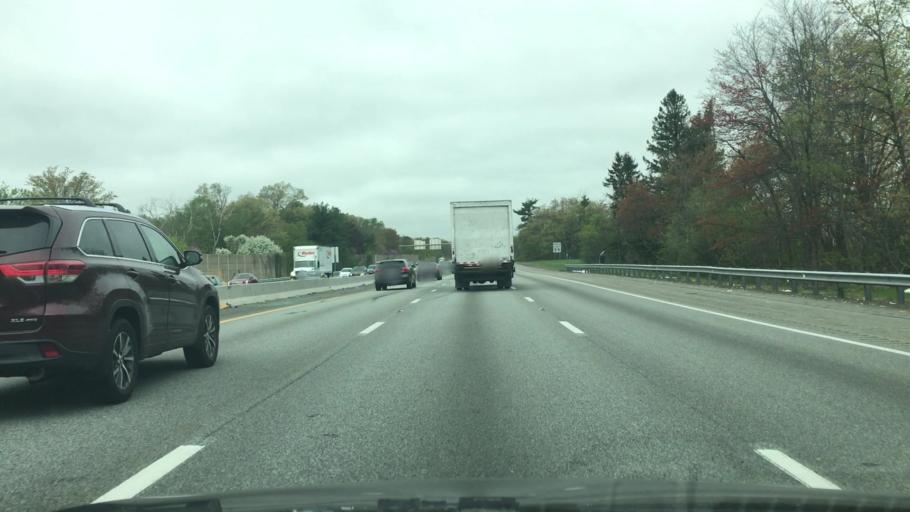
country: US
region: Massachusetts
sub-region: Essex County
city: Lynnfield
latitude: 42.5151
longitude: -71.0464
